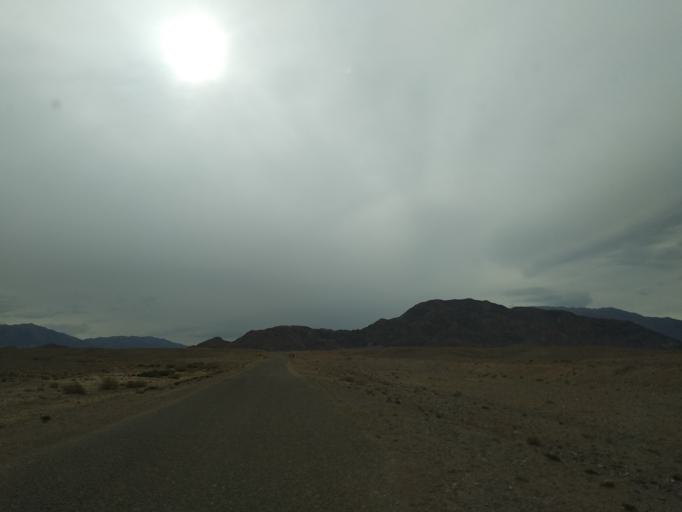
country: KG
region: Ysyk-Koel
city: Balykchy
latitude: 42.3202
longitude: 76.1793
